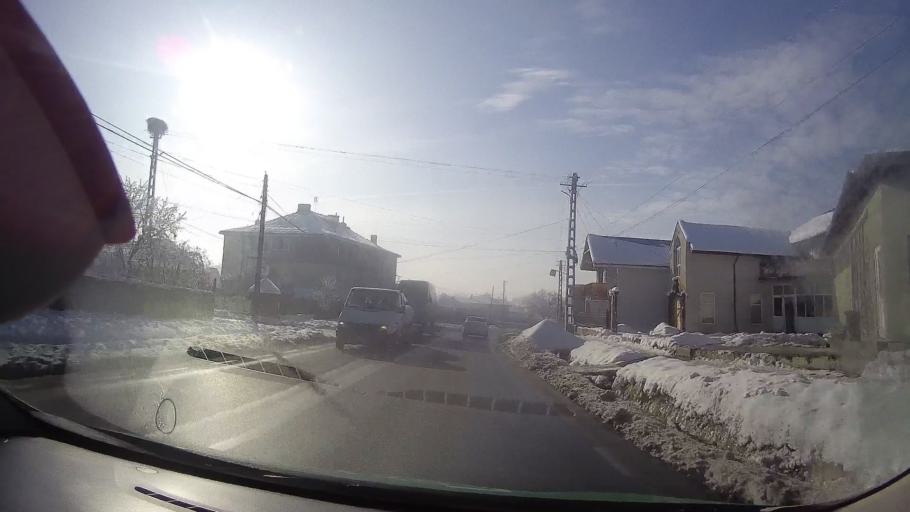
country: RO
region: Iasi
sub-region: Comuna Motca
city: Motca
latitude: 47.2403
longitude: 26.6065
